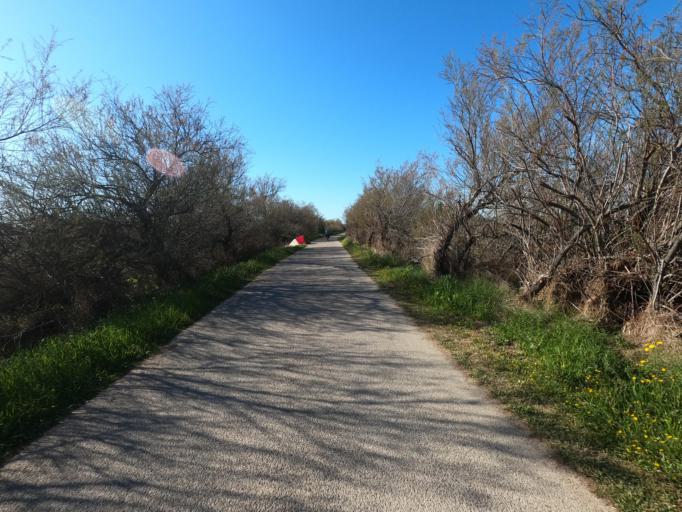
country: FR
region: Languedoc-Roussillon
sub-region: Departement de l'Herault
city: Palavas-les-Flots
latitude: 43.5370
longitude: 3.9051
